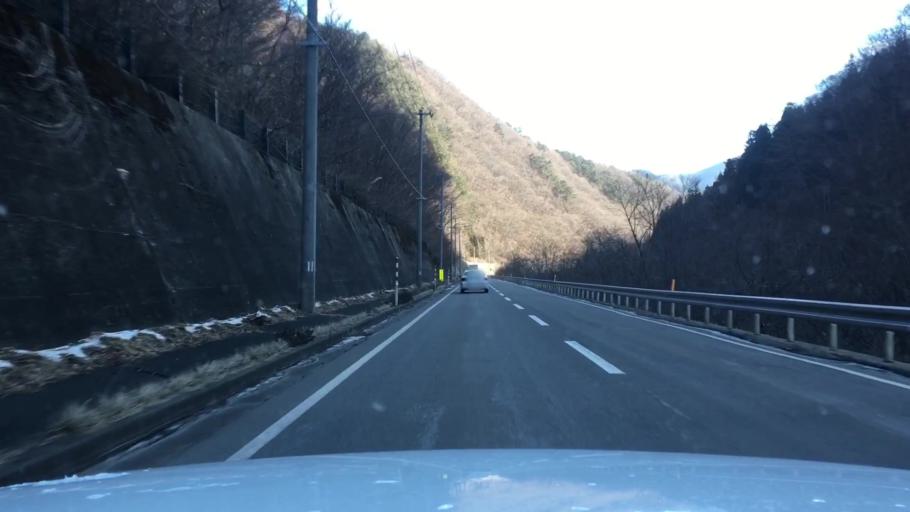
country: JP
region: Iwate
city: Tono
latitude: 39.6480
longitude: 141.5737
